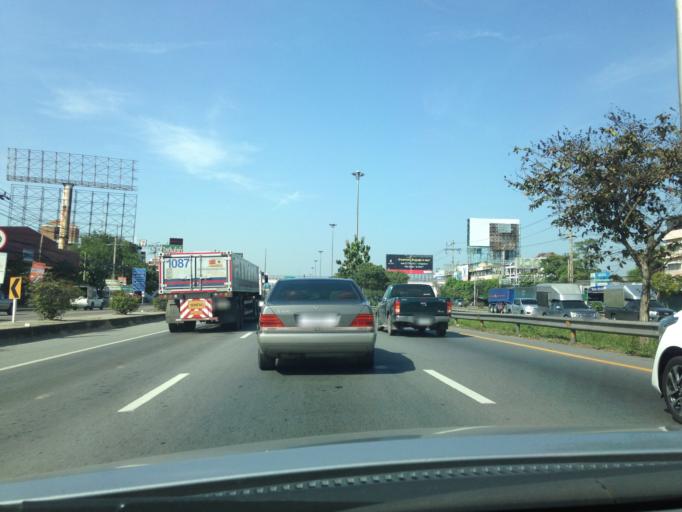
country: TH
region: Nonthaburi
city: Bang Yai
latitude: 13.8359
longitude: 100.4135
